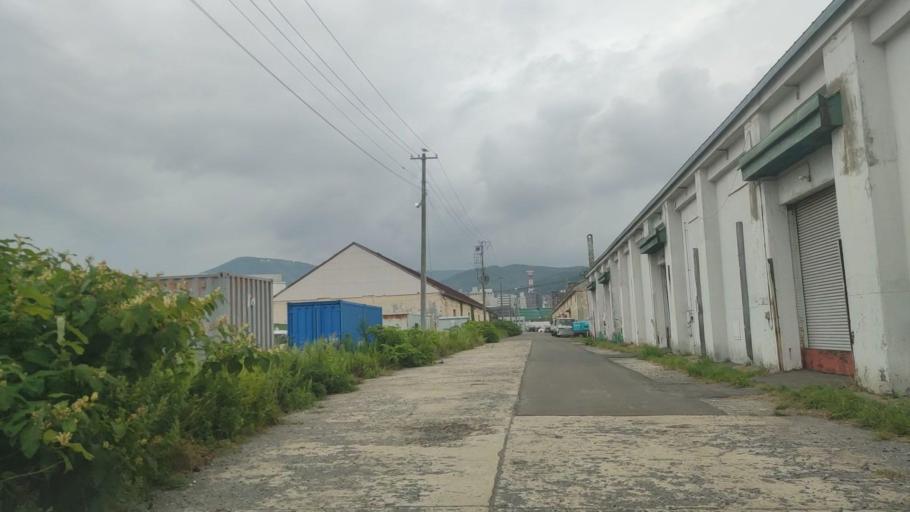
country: JP
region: Hokkaido
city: Otaru
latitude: 43.2000
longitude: 141.0077
